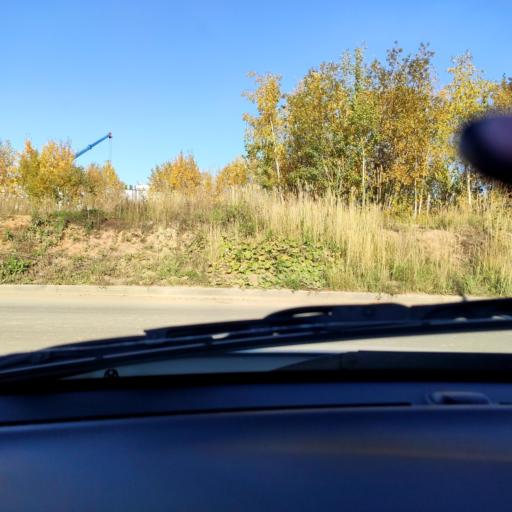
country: RU
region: Tatarstan
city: Stolbishchi
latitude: 55.7226
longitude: 49.1870
